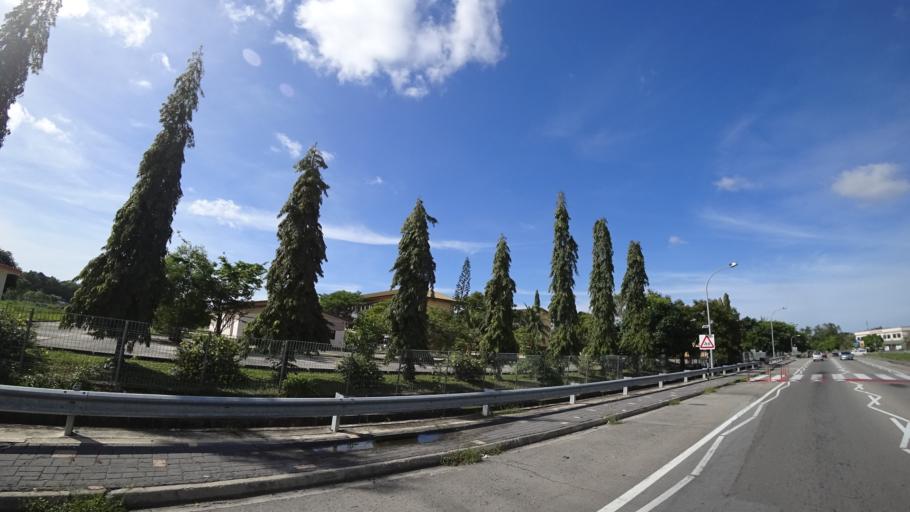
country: BN
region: Brunei and Muara
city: Bandar Seri Begawan
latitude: 4.9127
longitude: 114.9239
